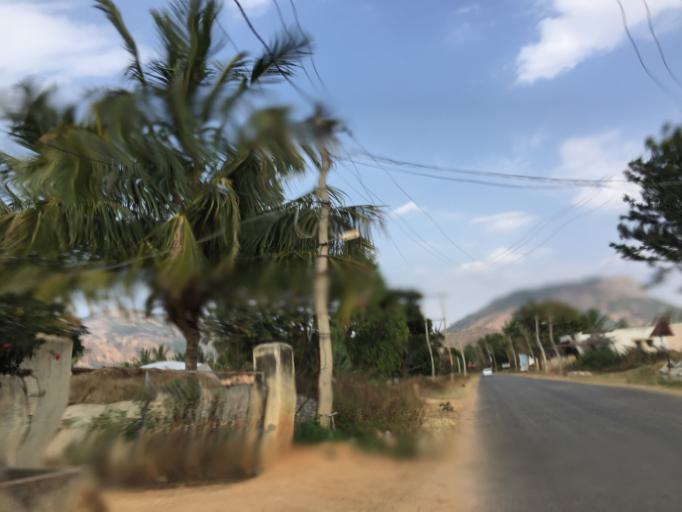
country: IN
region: Karnataka
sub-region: Chikkaballapur
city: Chik Ballapur
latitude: 13.3600
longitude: 77.6516
